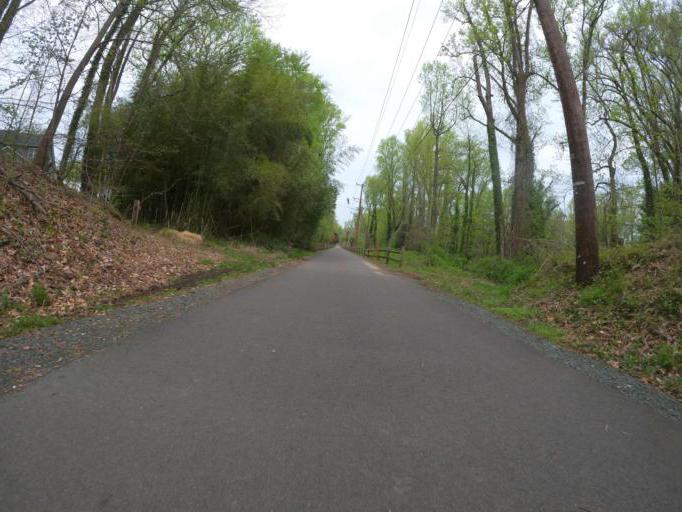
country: US
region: Maryland
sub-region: Anne Arundel County
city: Arnold
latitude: 39.0219
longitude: -76.5012
